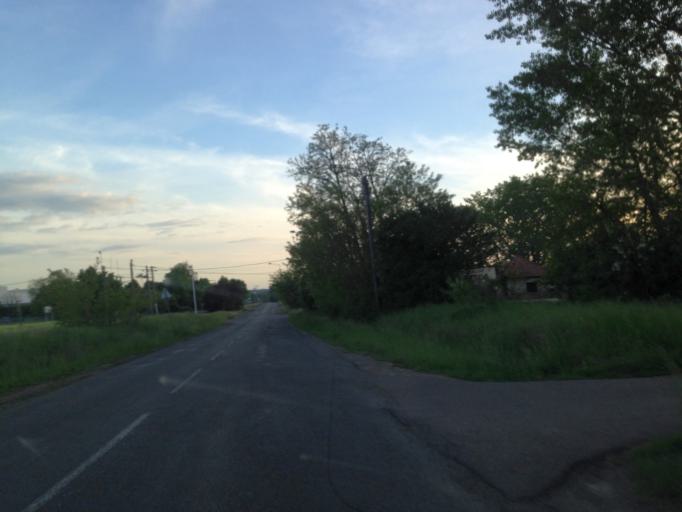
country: HU
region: Nograd
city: Paszto
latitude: 47.9335
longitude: 19.7151
